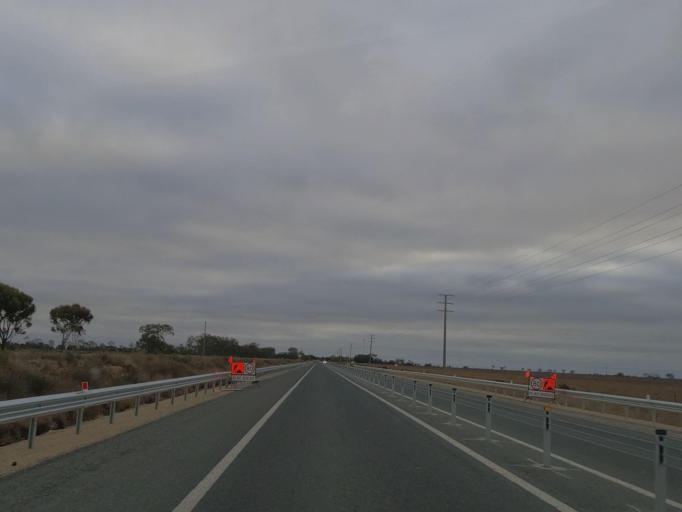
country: AU
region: Victoria
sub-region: Swan Hill
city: Swan Hill
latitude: -35.5427
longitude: 143.7558
